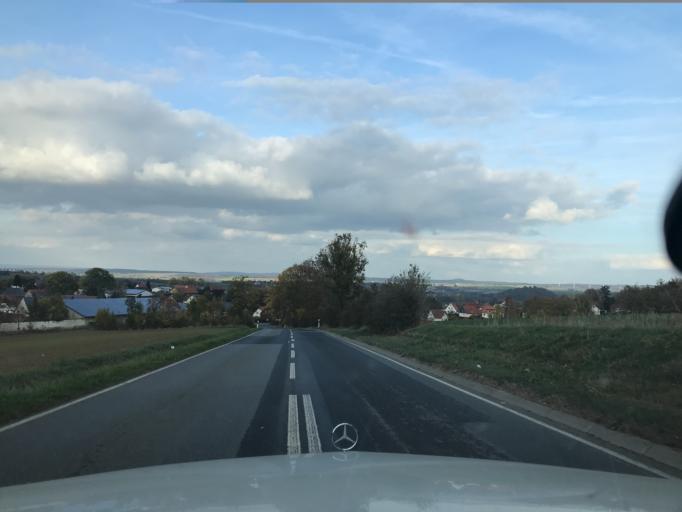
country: DE
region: Hesse
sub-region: Regierungsbezirk Kassel
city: Calden
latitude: 51.4301
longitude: 9.3795
